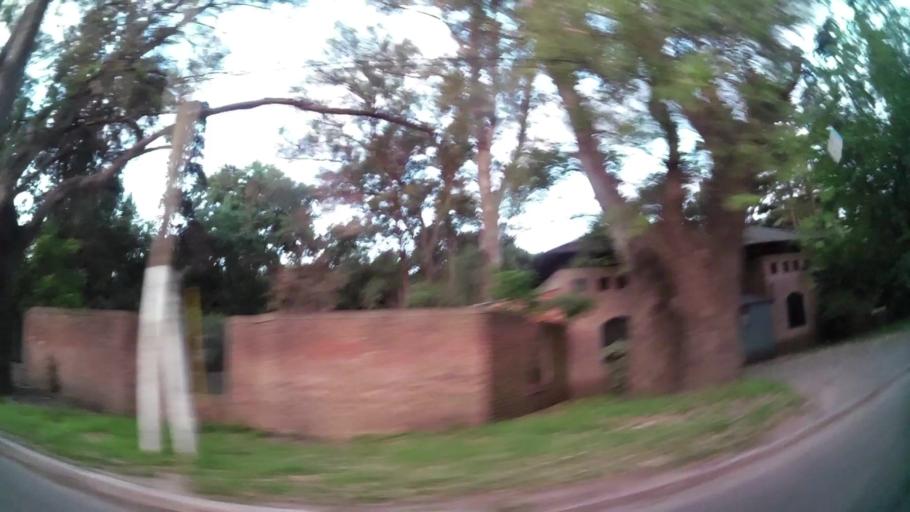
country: AR
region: Buenos Aires
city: Santa Catalina - Dique Lujan
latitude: -34.4815
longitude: -58.7807
